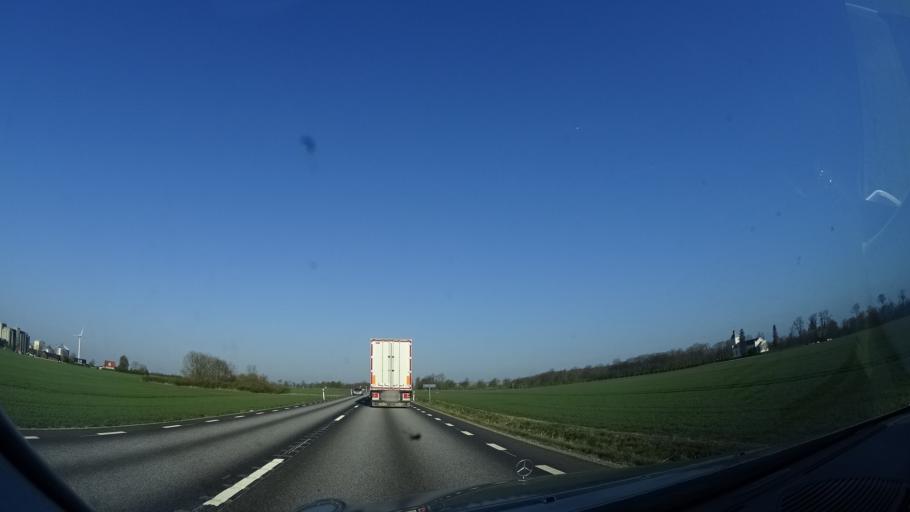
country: SE
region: Skane
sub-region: Eslovs Kommun
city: Eslov
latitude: 55.8608
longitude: 13.2474
